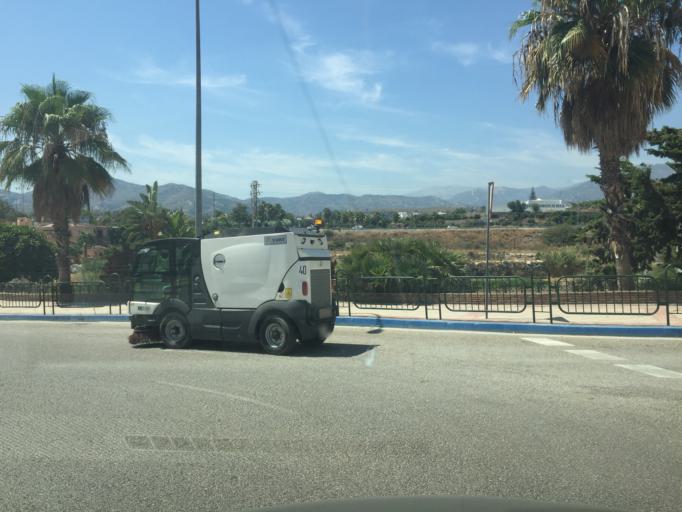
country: ES
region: Andalusia
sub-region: Provincia de Malaga
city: Nerja
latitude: 36.7480
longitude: -3.8804
